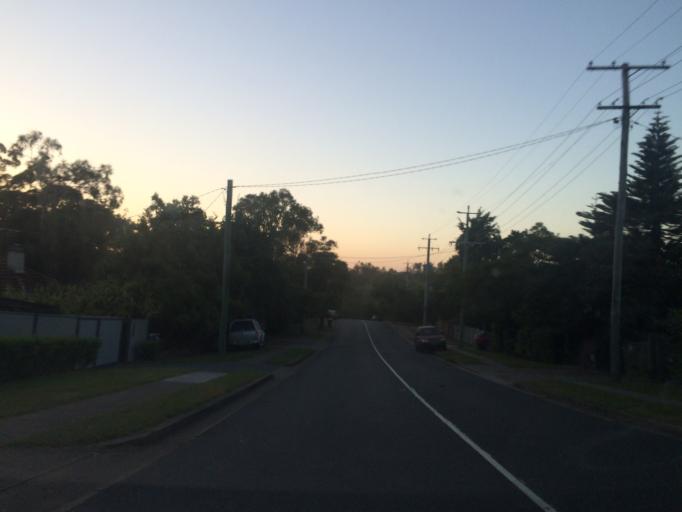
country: AU
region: Queensland
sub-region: Brisbane
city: Taringa
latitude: -27.4981
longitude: 152.9603
